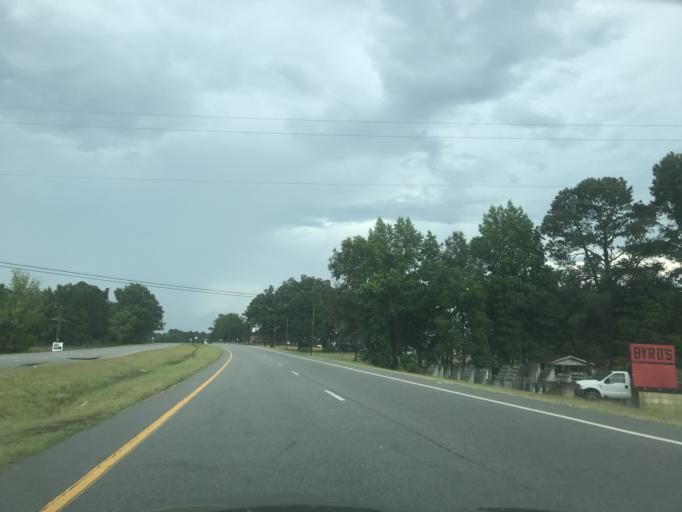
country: US
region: North Carolina
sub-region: Johnston County
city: Wilsons Mills
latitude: 35.5625
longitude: -78.3916
